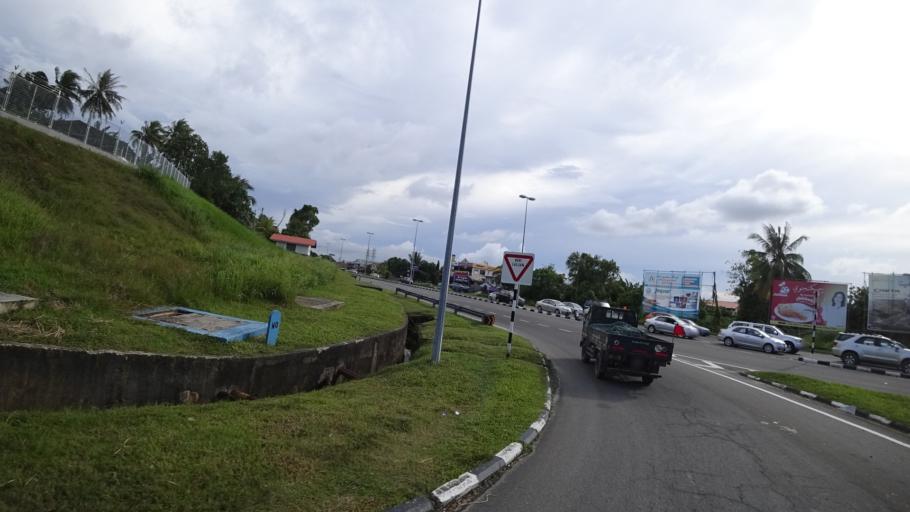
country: BN
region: Brunei and Muara
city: Bandar Seri Begawan
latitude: 4.8779
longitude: 114.8605
